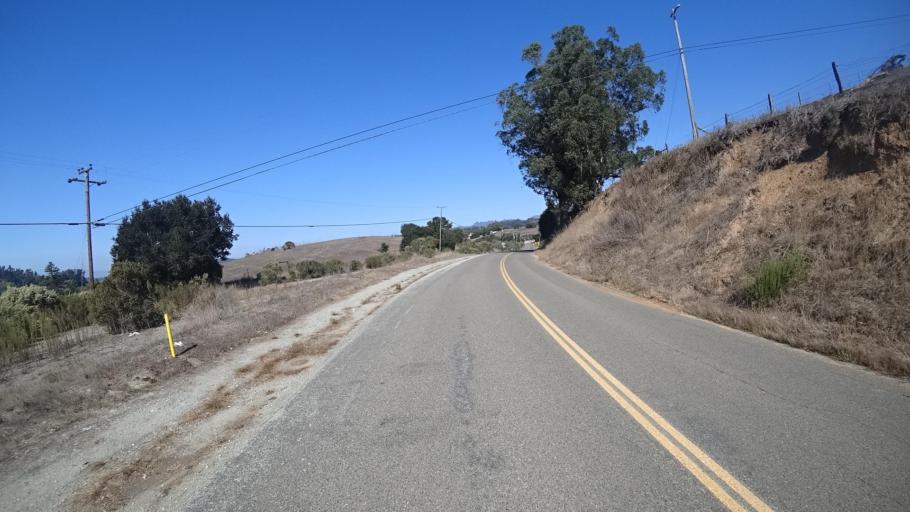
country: US
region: California
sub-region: San Benito County
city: Aromas
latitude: 36.8505
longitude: -121.6397
